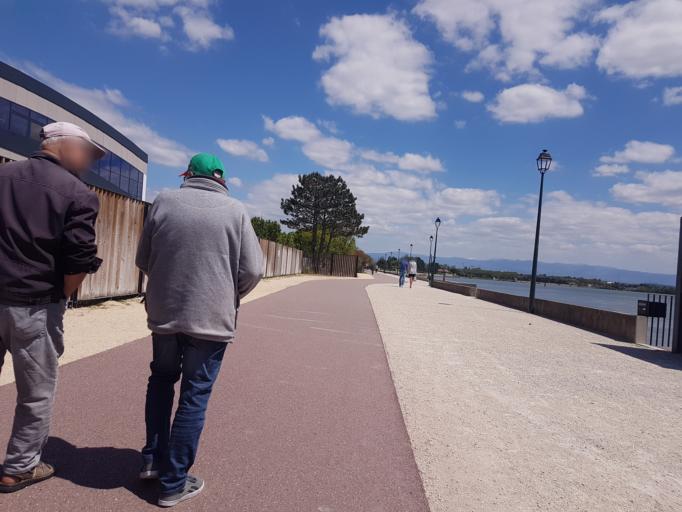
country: FR
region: Rhone-Alpes
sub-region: Departement de l'Ardeche
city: Tournon-sur-Rhone
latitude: 45.0671
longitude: 4.8456
